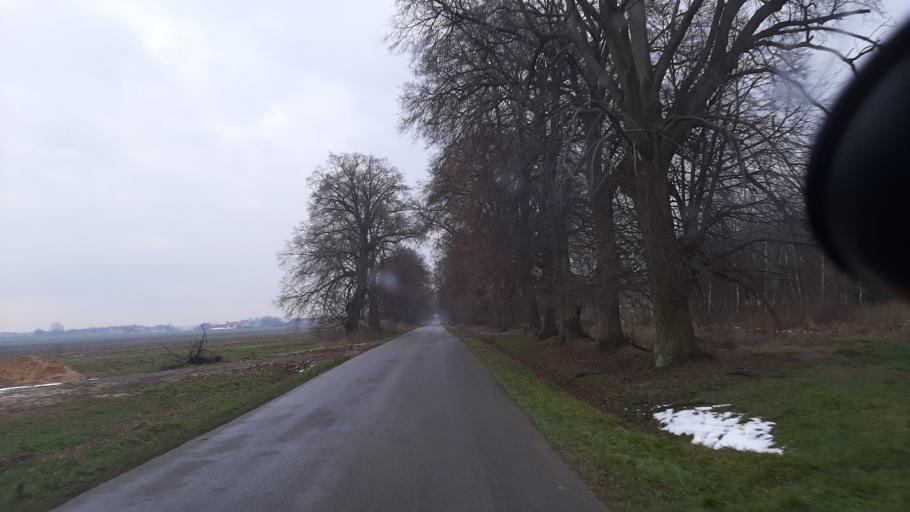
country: PL
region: Lublin Voivodeship
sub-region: Powiat lubelski
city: Jastkow
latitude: 51.3444
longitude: 22.5269
